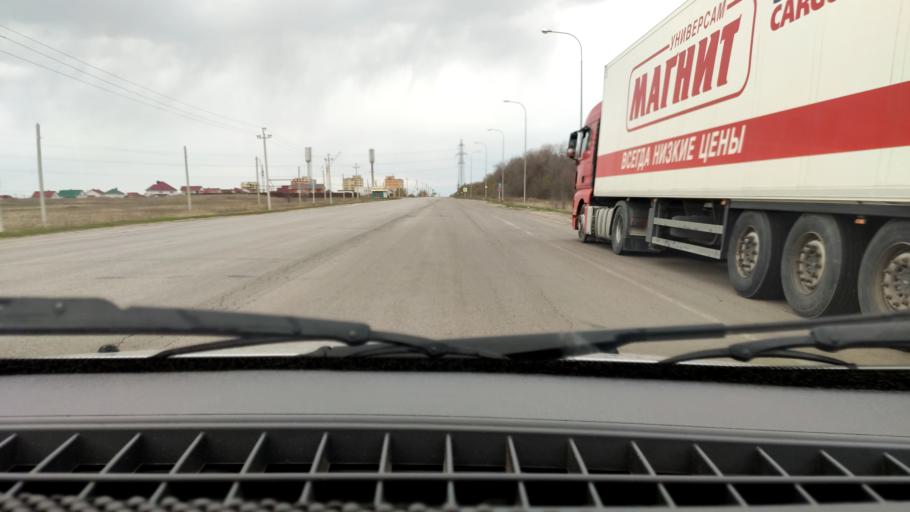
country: RU
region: Voronezj
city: Novaya Usman'
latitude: 51.6213
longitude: 39.3354
